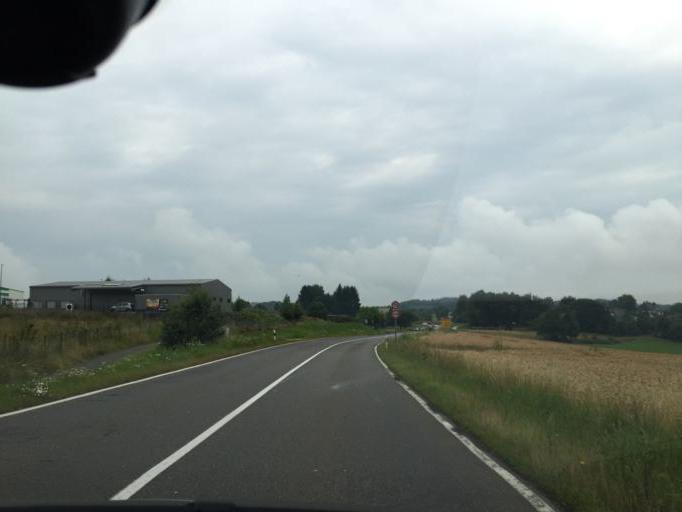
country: DE
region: Rheinland-Pfalz
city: Bonefeld
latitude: 50.5192
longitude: 7.4857
